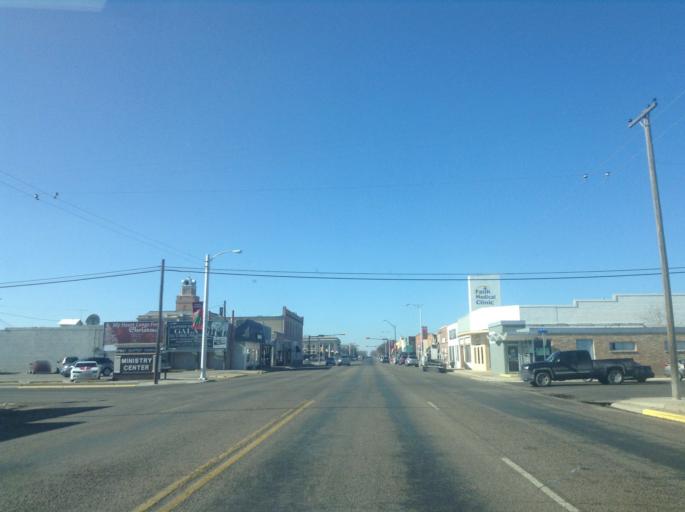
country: US
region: Texas
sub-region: Randall County
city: Canyon
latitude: 34.9799
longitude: -101.9259
